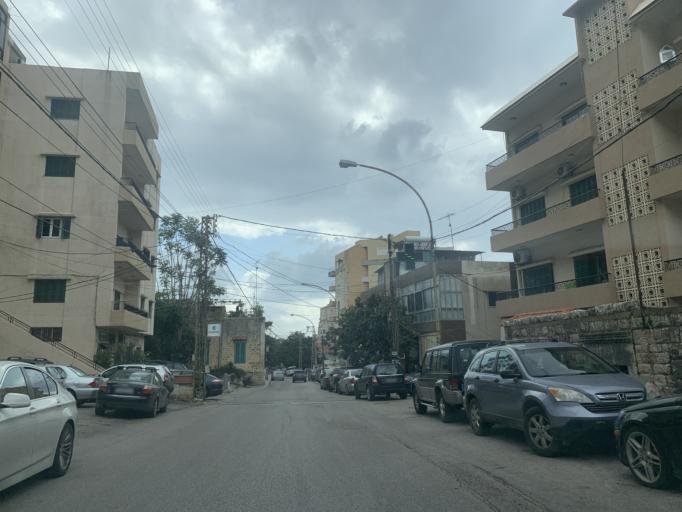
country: LB
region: Mont-Liban
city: Djounie
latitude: 33.9837
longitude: 35.6400
